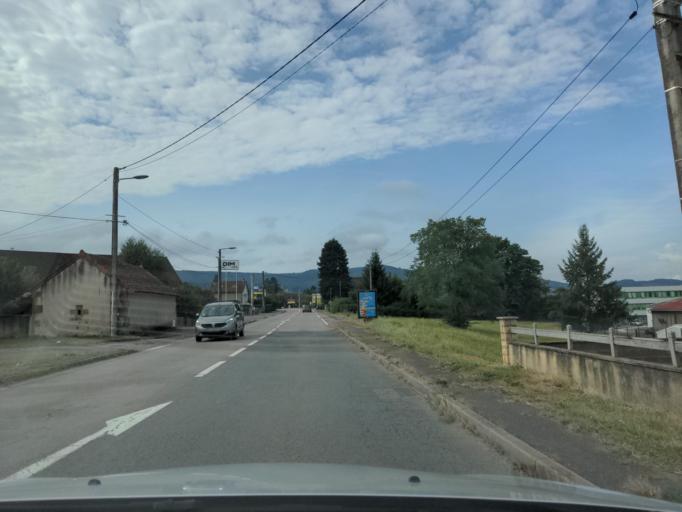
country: FR
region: Bourgogne
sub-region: Departement de Saone-et-Loire
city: Autun
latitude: 46.9699
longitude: 4.3057
